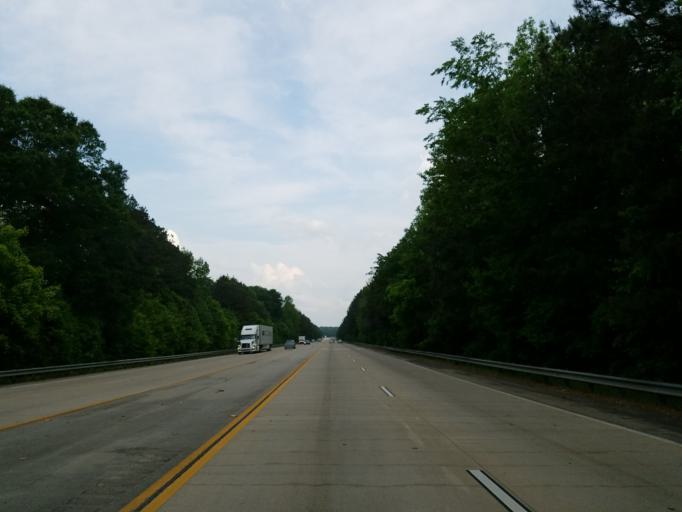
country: US
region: Georgia
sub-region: Cobb County
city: Powder Springs
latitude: 33.8287
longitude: -84.6680
